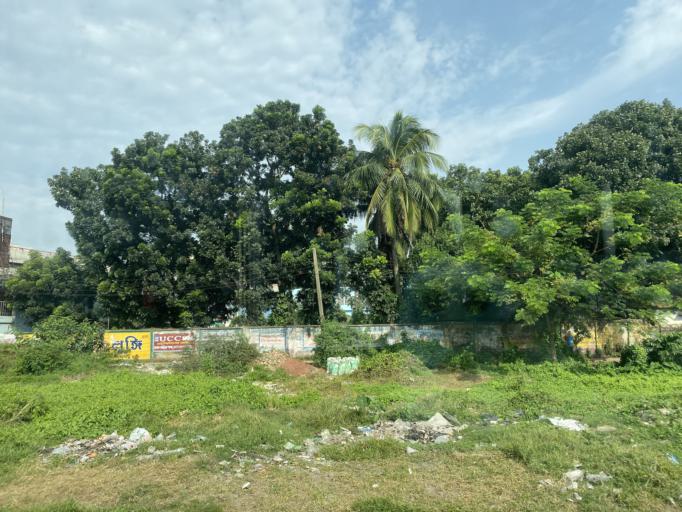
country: BD
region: Dhaka
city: Bhairab Bazar
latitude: 23.9679
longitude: 91.1123
